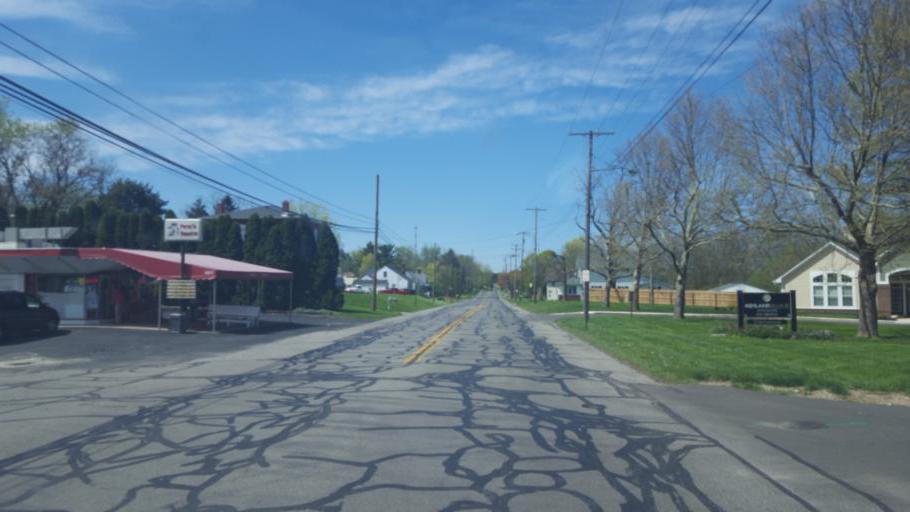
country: US
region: Ohio
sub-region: Ashland County
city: Ashland
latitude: 40.8803
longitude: -82.3209
